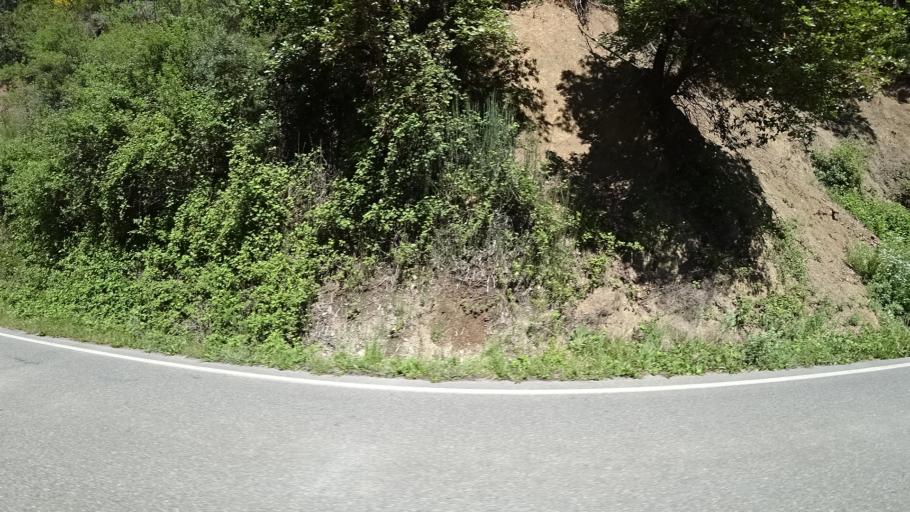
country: US
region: California
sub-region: Trinity County
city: Hayfork
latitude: 40.7480
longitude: -123.2724
